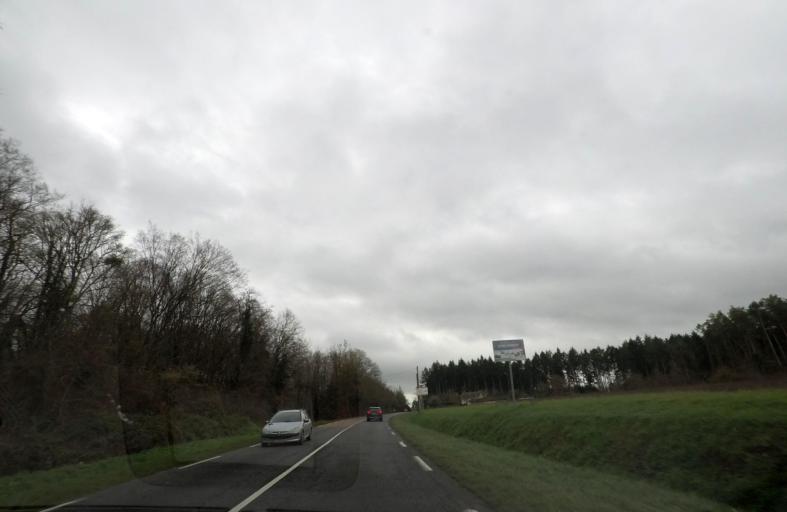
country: FR
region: Centre
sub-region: Departement du Loir-et-Cher
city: Cour-Cheverny
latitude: 47.5305
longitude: 1.4252
